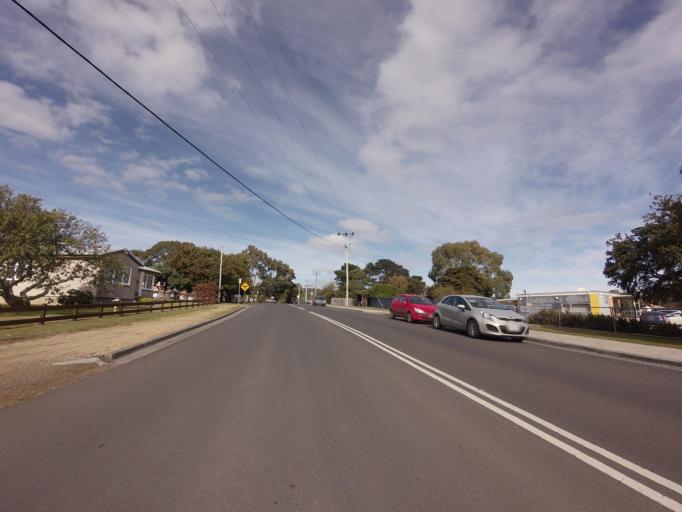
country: AU
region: Tasmania
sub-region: Clarence
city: Sandford
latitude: -43.0968
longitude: 147.7435
